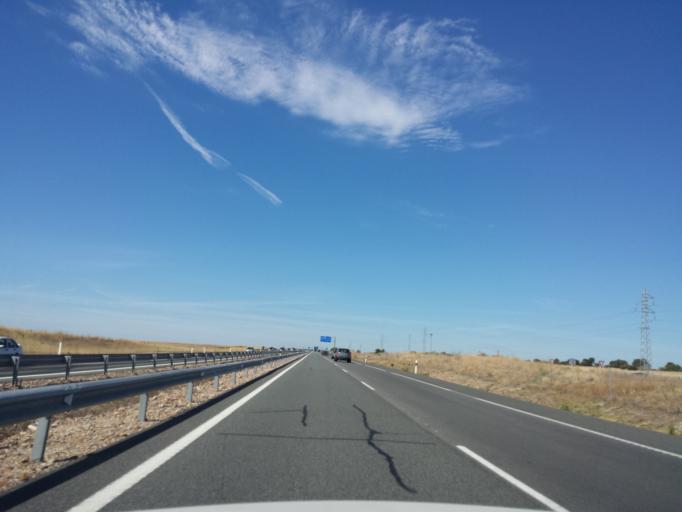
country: ES
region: Castille-La Mancha
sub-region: Province of Toledo
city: Calera y Chozas
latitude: 39.9253
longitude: -5.0268
